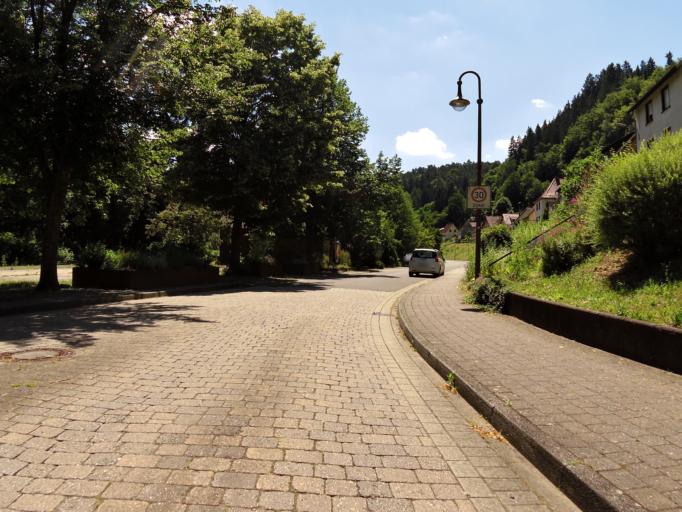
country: DE
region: Rheinland-Pfalz
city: Elmstein
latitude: 49.3493
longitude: 7.9429
